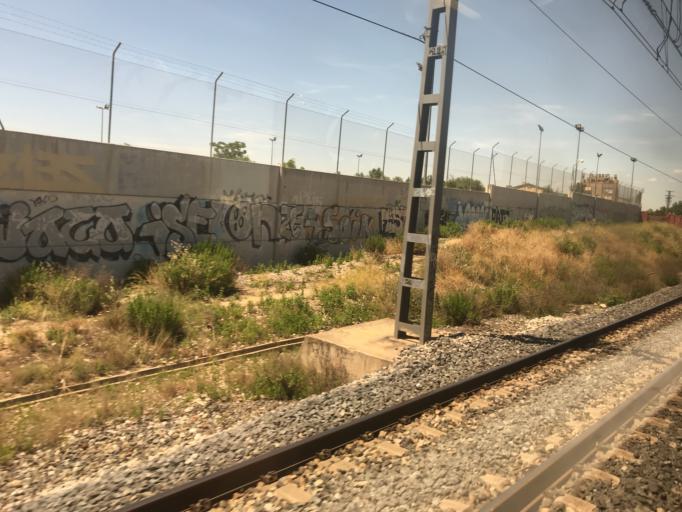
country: ES
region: Madrid
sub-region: Provincia de Madrid
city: Villaverde
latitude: 40.3383
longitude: -3.6841
